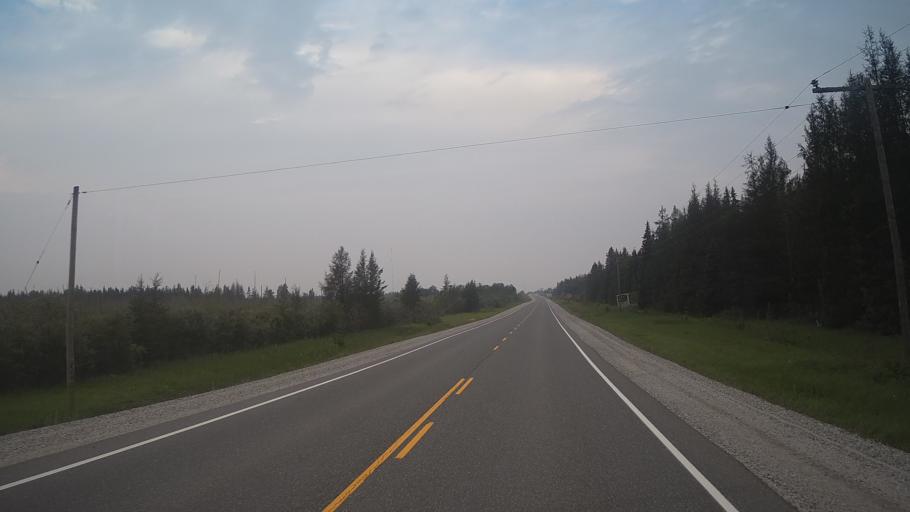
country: CA
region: Ontario
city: Hearst
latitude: 49.6620
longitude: -83.4846
